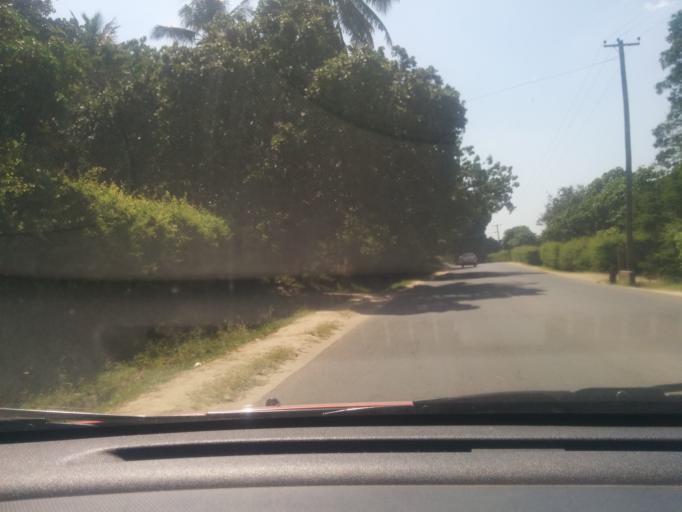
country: TZ
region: Dar es Salaam
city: Magomeni
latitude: -6.7704
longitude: 39.2137
